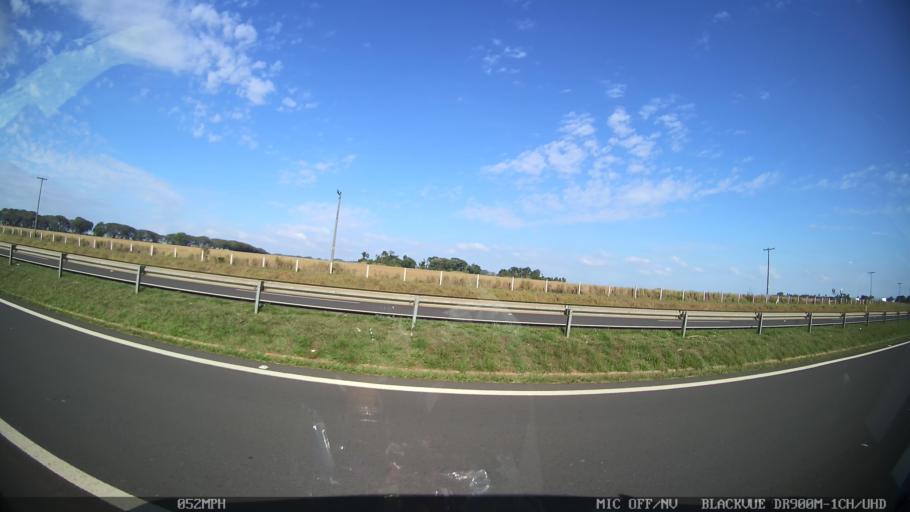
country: BR
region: Sao Paulo
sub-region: Iracemapolis
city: Iracemapolis
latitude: -22.6514
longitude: -47.5158
